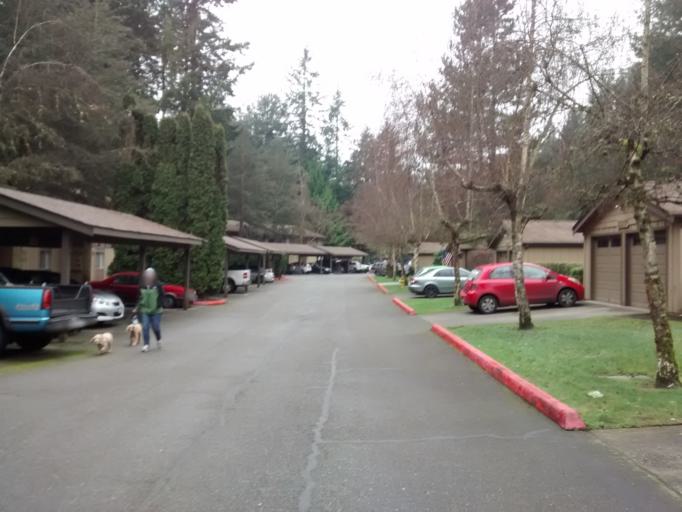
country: US
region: Washington
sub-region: Kitsap County
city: Parkwood
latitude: 47.5218
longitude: -122.6059
